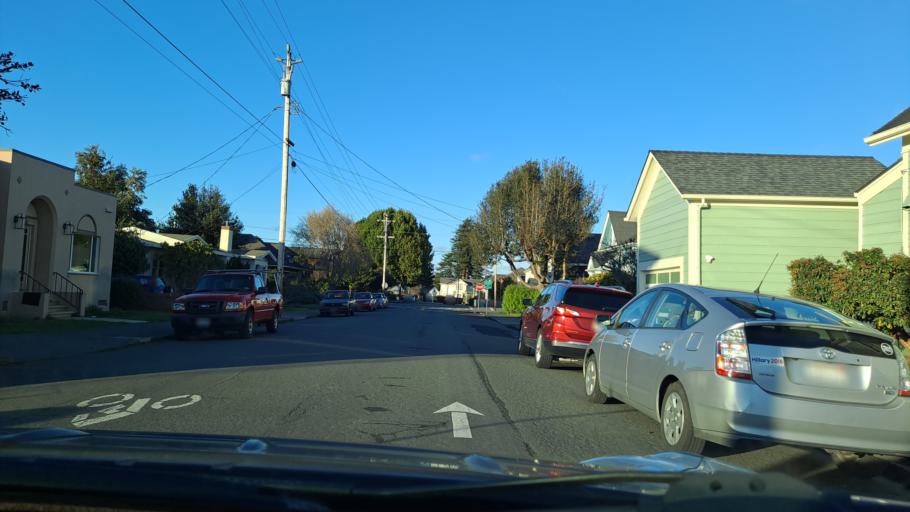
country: US
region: California
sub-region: Humboldt County
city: Arcata
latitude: 40.8741
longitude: -124.0860
